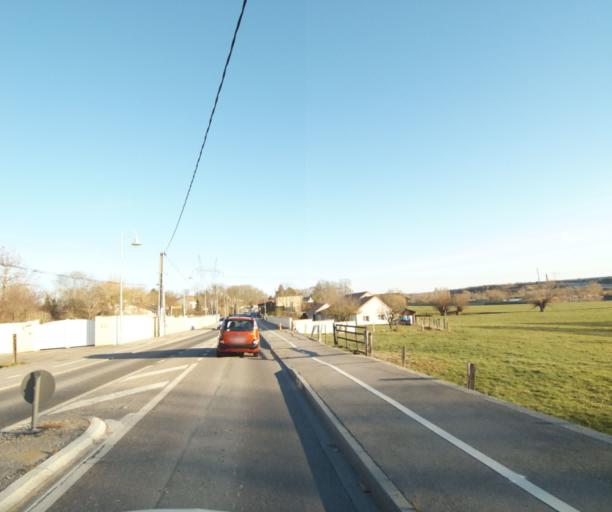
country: FR
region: Lorraine
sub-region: Departement de Meurthe-et-Moselle
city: Art-sur-Meurthe
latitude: 48.6591
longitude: 6.2594
